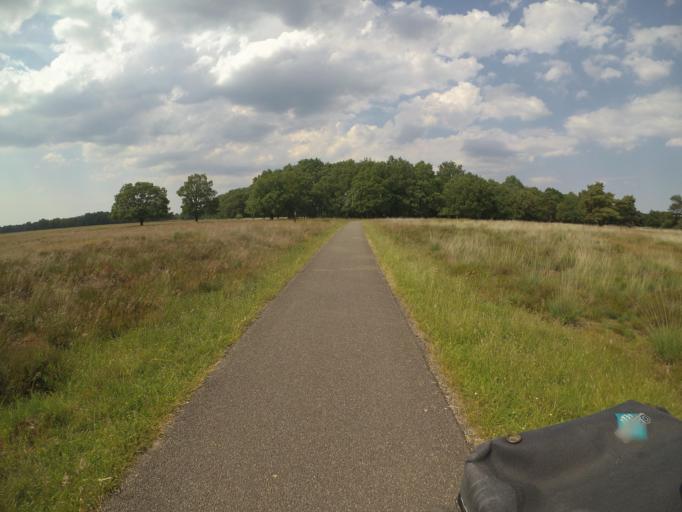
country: NL
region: Drenthe
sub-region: Gemeente Assen
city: Assen
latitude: 52.9244
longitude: 6.5019
